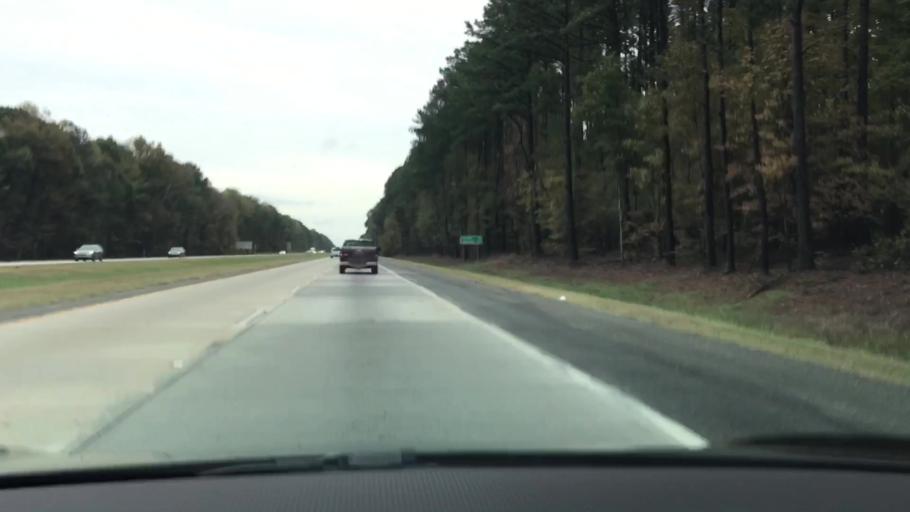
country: US
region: Georgia
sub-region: Greene County
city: Greensboro
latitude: 33.5466
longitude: -83.1884
